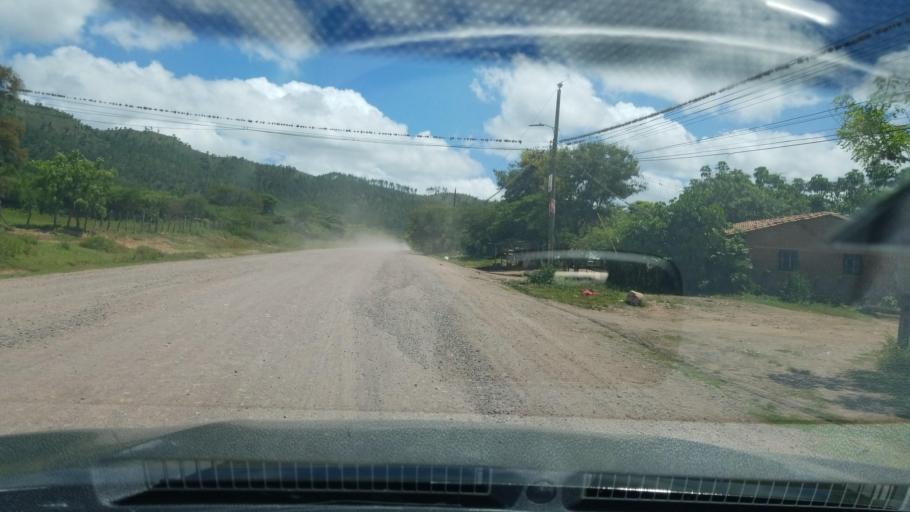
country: HN
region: Francisco Morazan
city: San Juan de Flores
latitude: 14.3316
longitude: -87.0460
